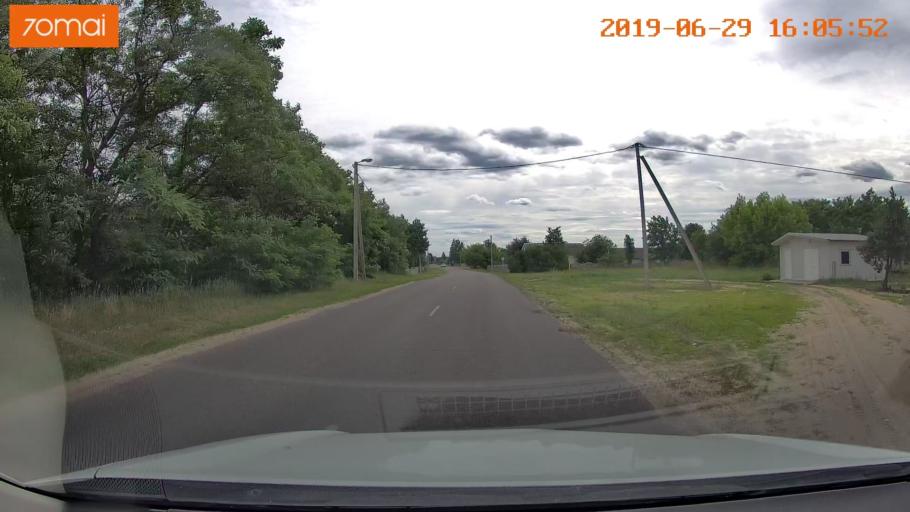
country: BY
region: Brest
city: Luninyets
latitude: 52.2132
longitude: 27.0166
